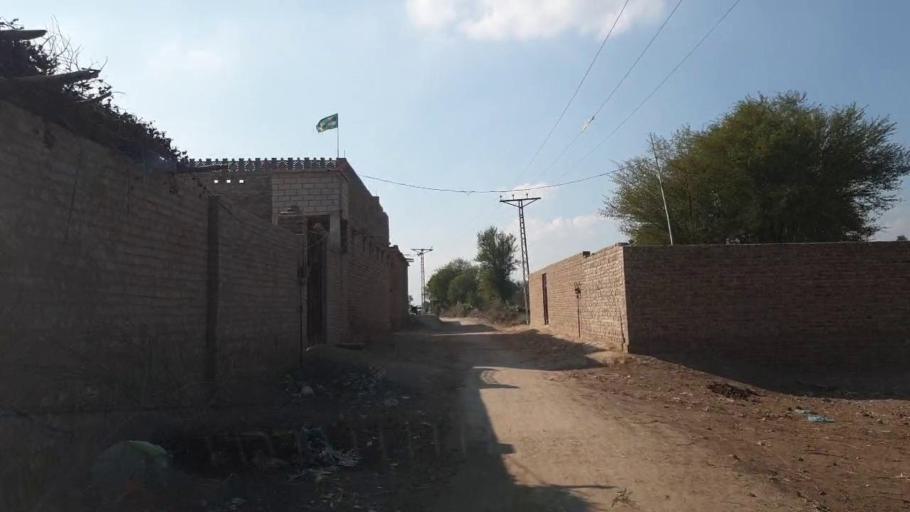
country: PK
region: Sindh
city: Shahpur Chakar
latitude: 26.1023
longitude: 68.5659
